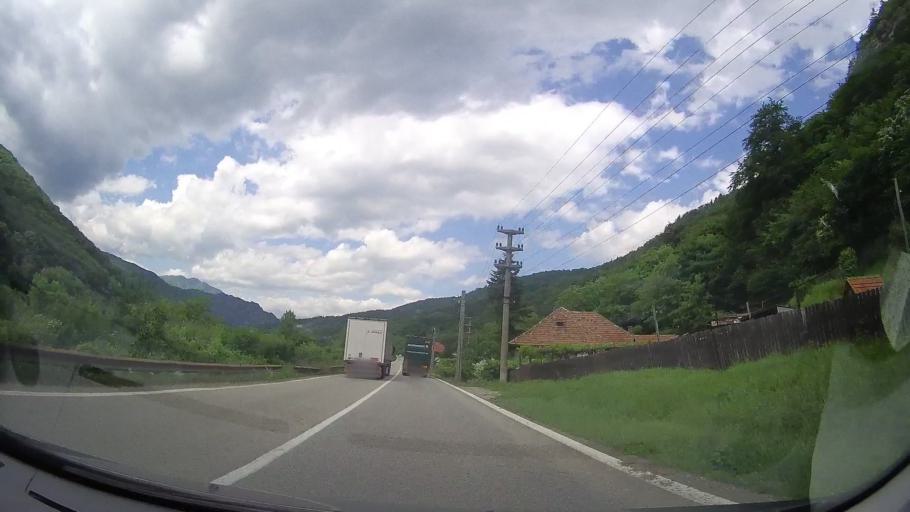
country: RO
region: Valcea
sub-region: Oras Calimanesti
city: Jiblea Veche
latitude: 45.2540
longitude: 24.3384
